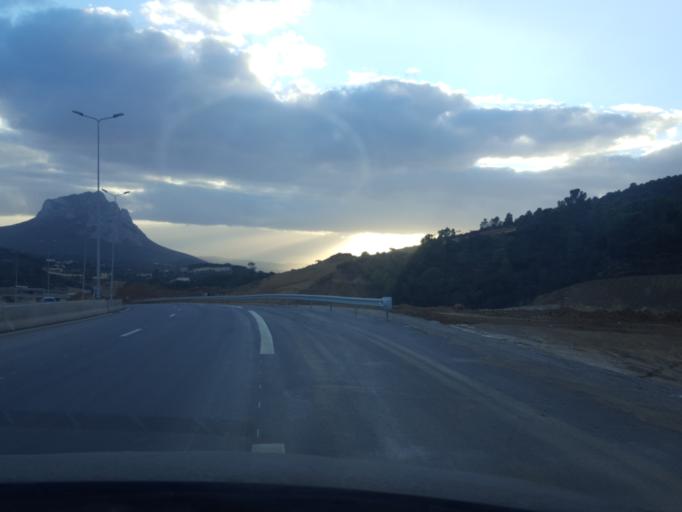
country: TN
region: Tunis
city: Hammam-Lif
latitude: 36.6520
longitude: 10.3699
